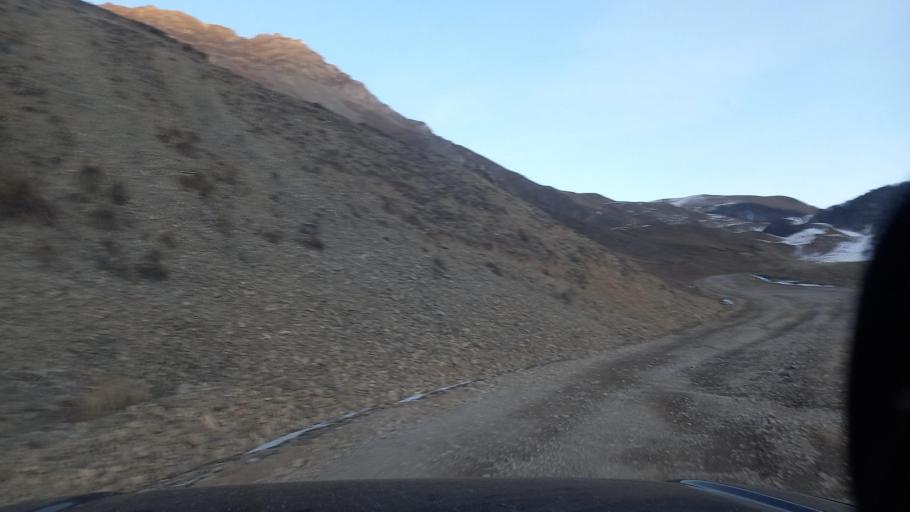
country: RU
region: Ingushetiya
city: Dzhayrakh
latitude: 42.8399
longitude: 44.5406
